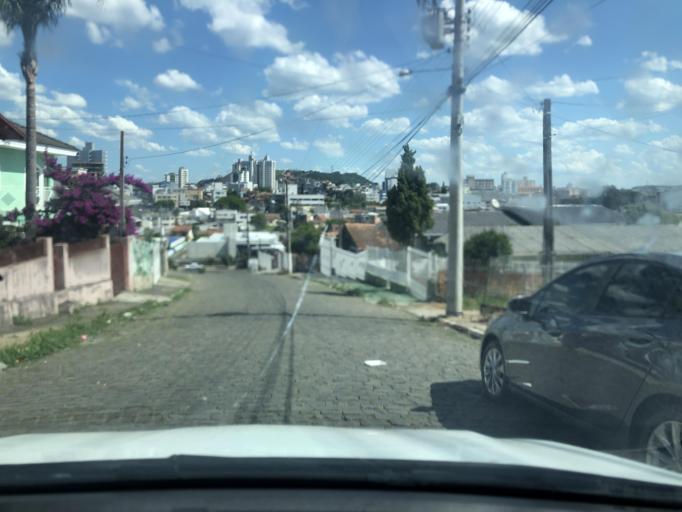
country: BR
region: Santa Catarina
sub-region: Lages
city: Lages
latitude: -27.8116
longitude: -50.3342
